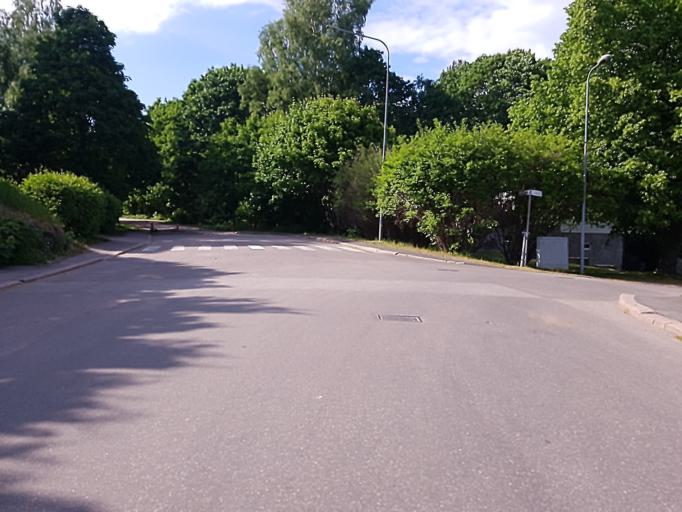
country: FI
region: Uusimaa
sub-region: Helsinki
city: Helsinki
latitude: 60.2387
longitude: 24.9697
